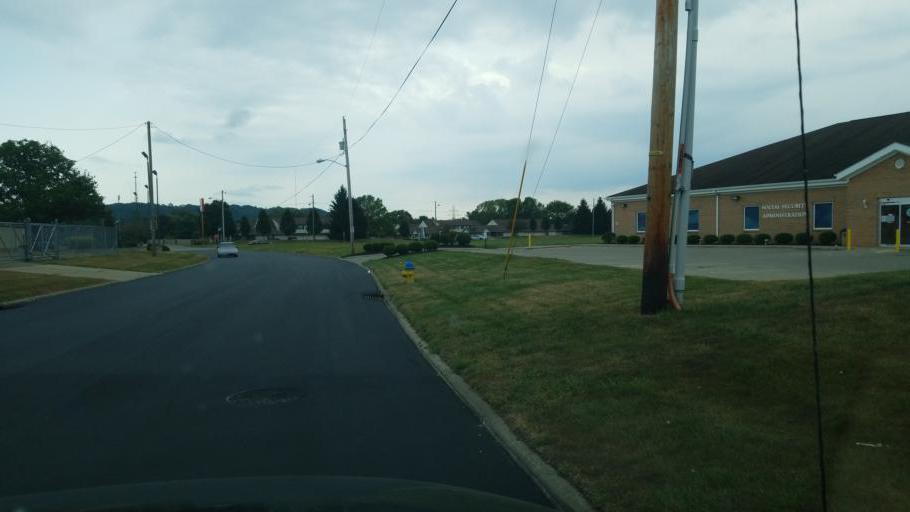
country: US
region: Ohio
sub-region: Licking County
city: Newark
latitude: 40.0961
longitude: -82.4283
